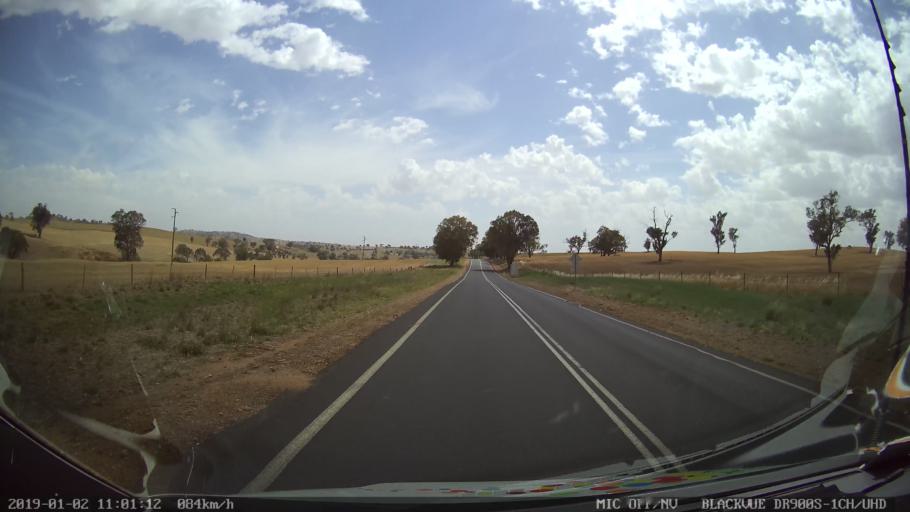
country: AU
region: New South Wales
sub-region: Young
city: Young
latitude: -34.6004
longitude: 148.3179
